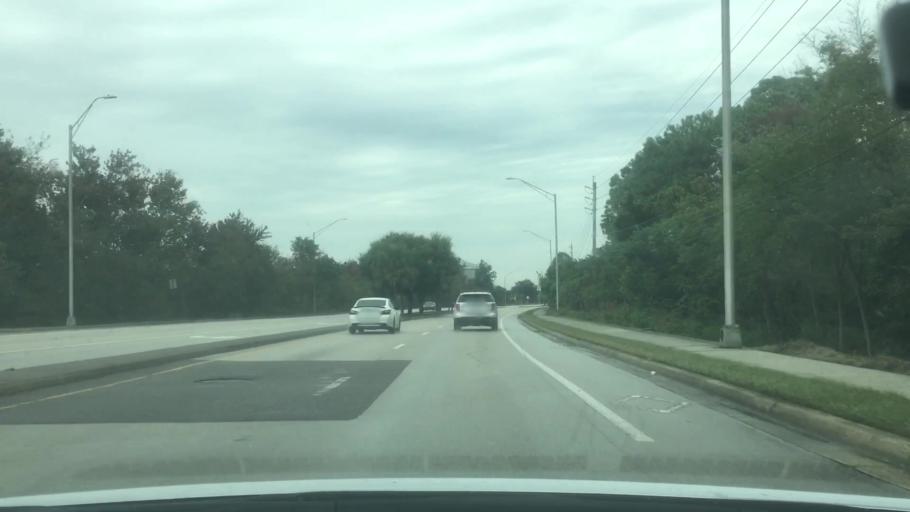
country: US
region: Florida
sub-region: Duval County
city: Jacksonville
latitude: 30.3343
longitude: -81.5467
